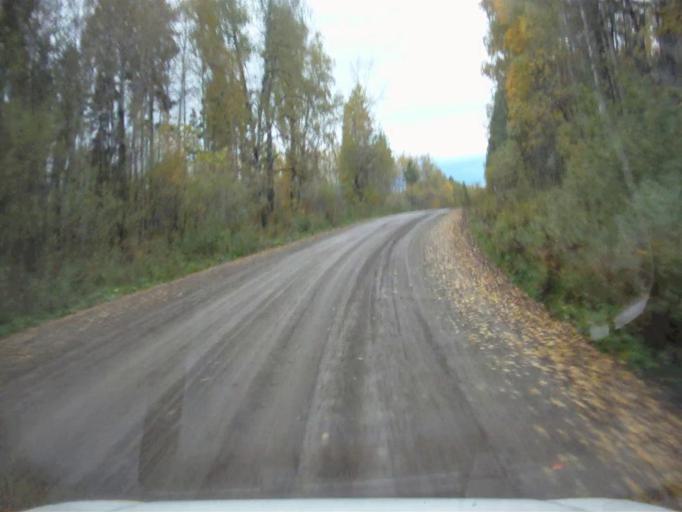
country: RU
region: Chelyabinsk
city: Nyazepetrovsk
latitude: 56.1159
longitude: 59.3679
